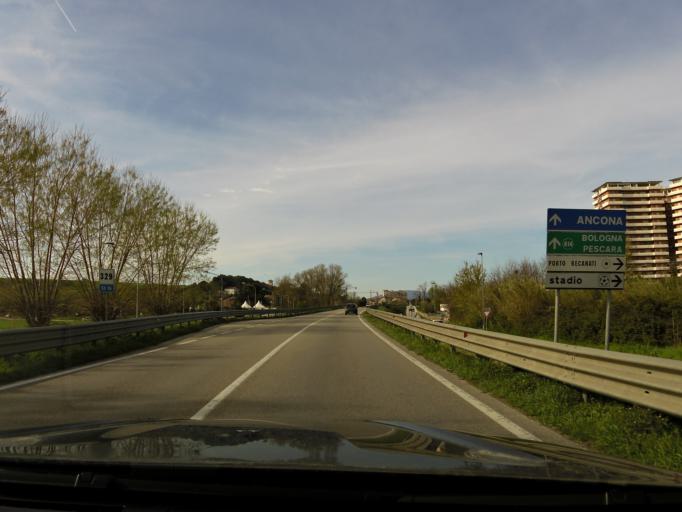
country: IT
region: The Marches
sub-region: Provincia di Macerata
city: Porto Recanati
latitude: 43.4186
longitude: 13.6660
